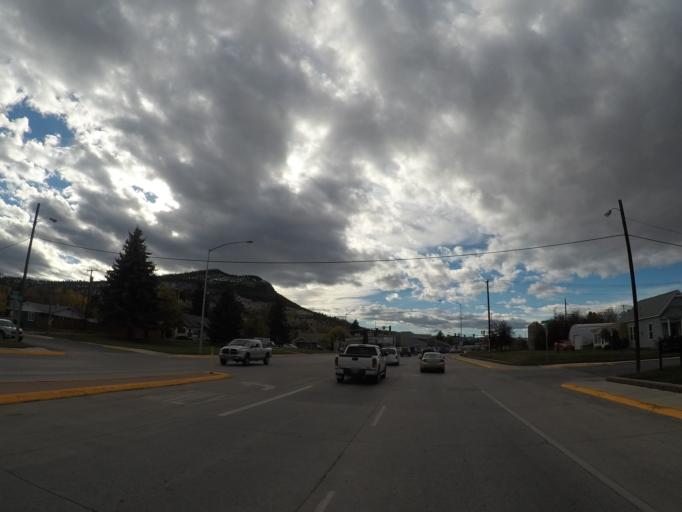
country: US
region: Montana
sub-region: Lewis and Clark County
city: Helena
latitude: 46.5981
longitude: -112.0396
